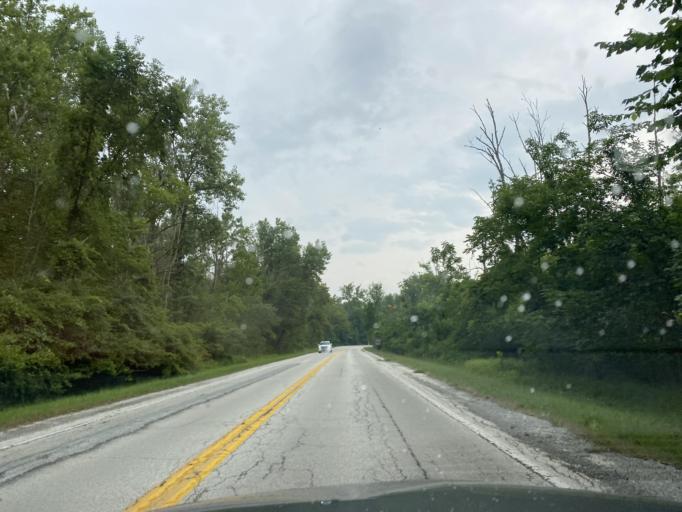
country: US
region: Ohio
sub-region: Summit County
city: Fairlawn
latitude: 41.1785
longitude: -81.5818
